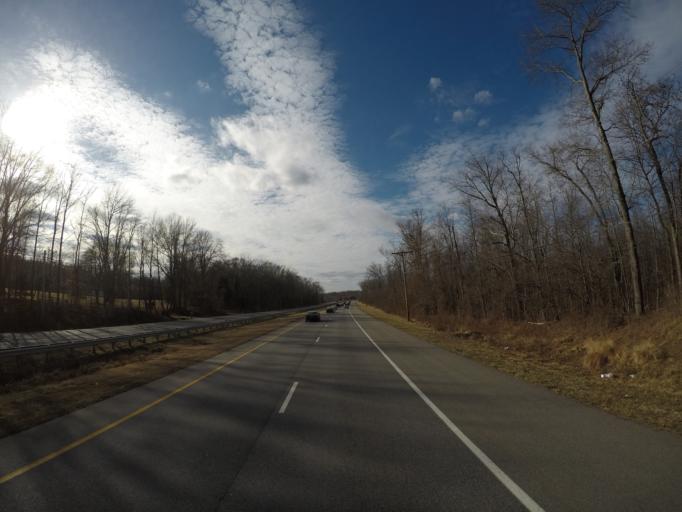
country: US
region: Maryland
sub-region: Prince George's County
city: Accokeek
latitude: 38.6522
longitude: -76.9892
